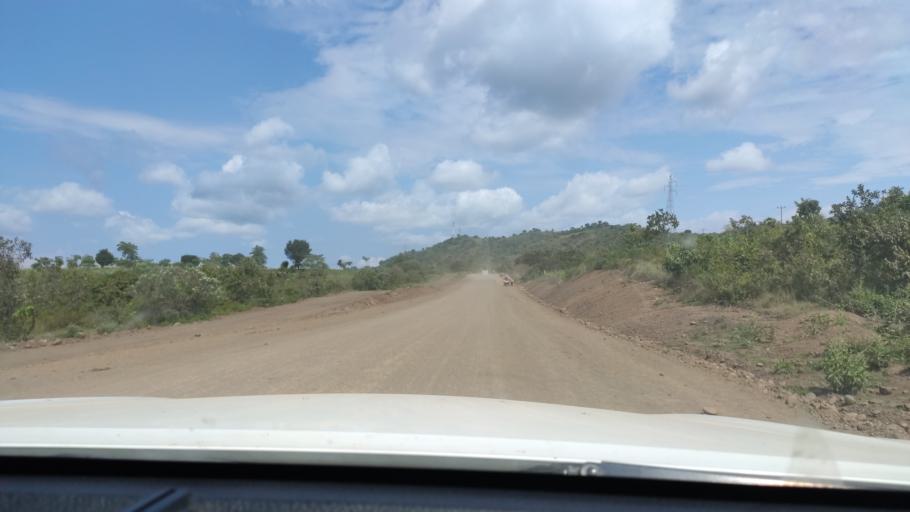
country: ET
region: Southern Nations, Nationalities, and People's Region
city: Felege Neway
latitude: 6.3914
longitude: 37.0571
